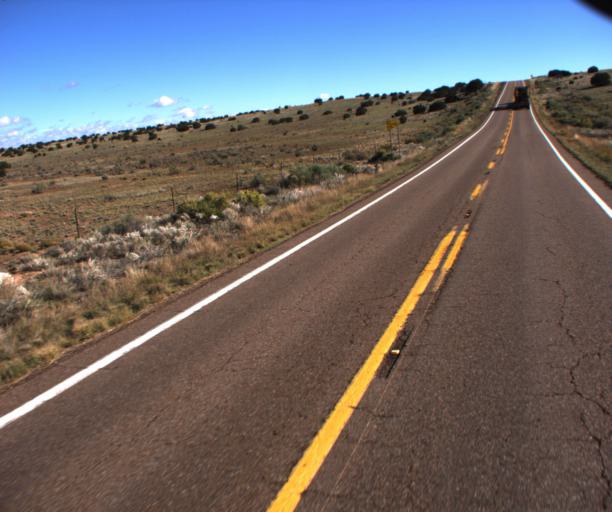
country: US
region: Arizona
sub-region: Apache County
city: Saint Johns
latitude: 34.4964
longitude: -109.5078
